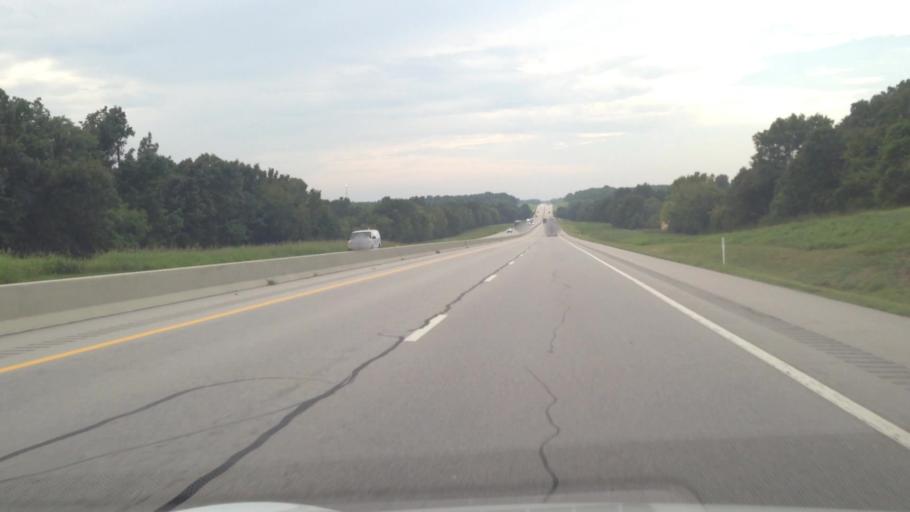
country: US
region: Kansas
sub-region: Cherokee County
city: Baxter Springs
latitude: 36.9296
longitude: -94.7288
